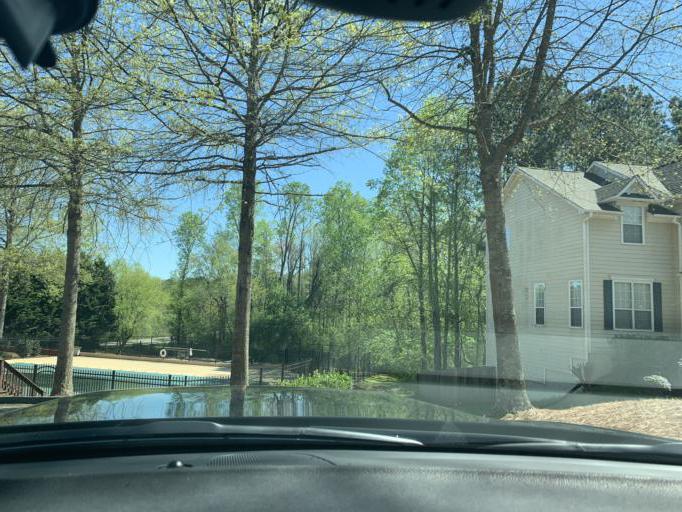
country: US
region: Georgia
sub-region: Fulton County
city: Milton
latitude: 34.1341
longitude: -84.2192
